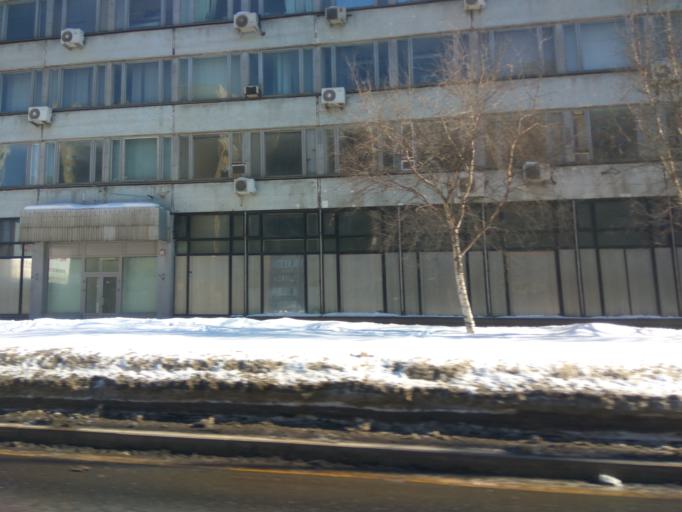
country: RU
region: Moscow
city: Taganskiy
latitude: 55.7379
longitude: 37.6547
